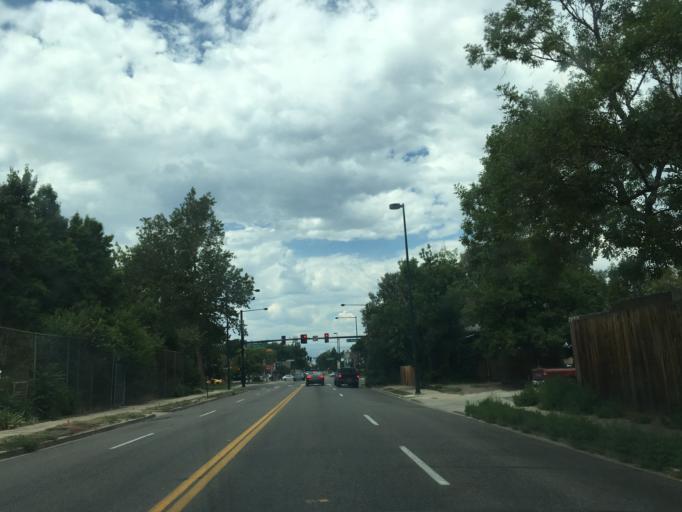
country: US
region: Colorado
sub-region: Denver County
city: Denver
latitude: 39.7112
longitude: -104.9712
